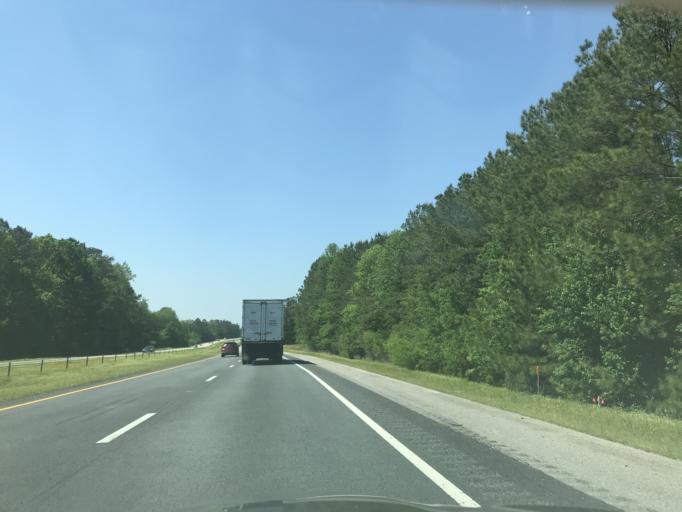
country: US
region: North Carolina
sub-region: Johnston County
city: Benson
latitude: 35.3782
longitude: -78.5060
